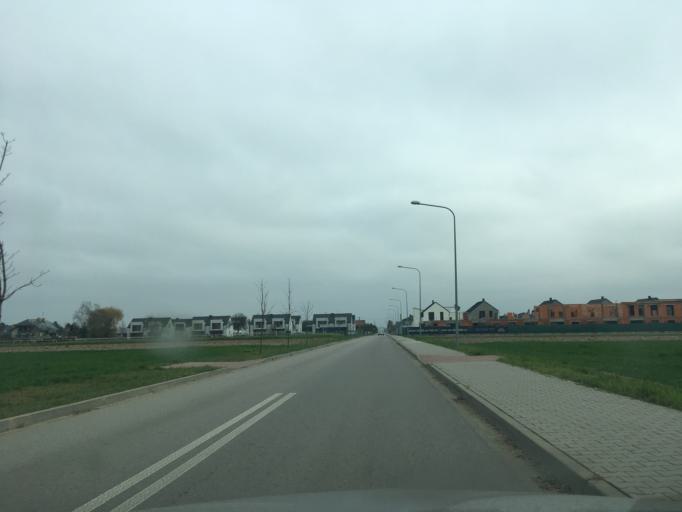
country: PL
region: Masovian Voivodeship
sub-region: Powiat piaseczynski
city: Lesznowola
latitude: 52.0850
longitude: 20.9407
